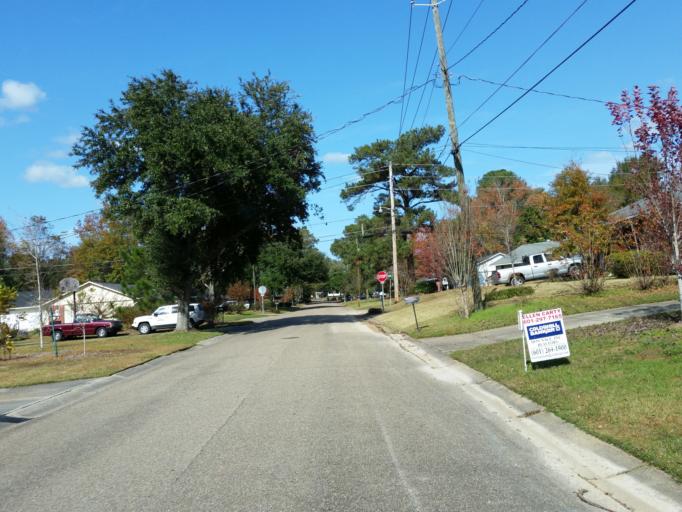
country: US
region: Mississippi
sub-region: Lamar County
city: West Hattiesburg
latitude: 31.3082
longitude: -89.3339
